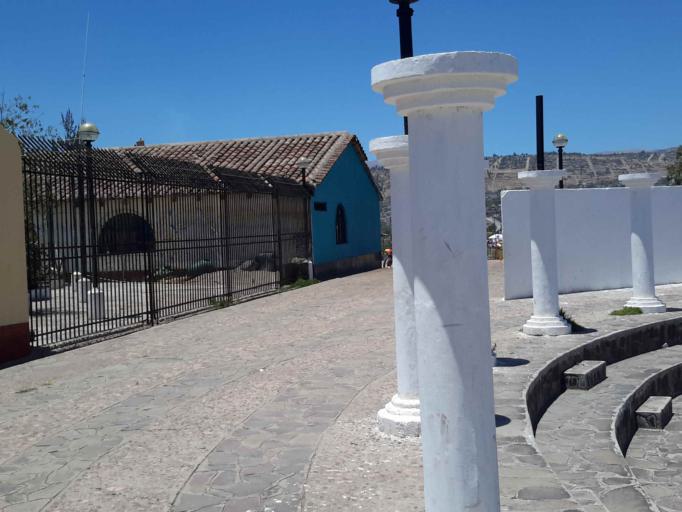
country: PE
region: Ayacucho
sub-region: Provincia de Huamanga
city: Carmen Alto
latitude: -13.1717
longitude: -74.2221
